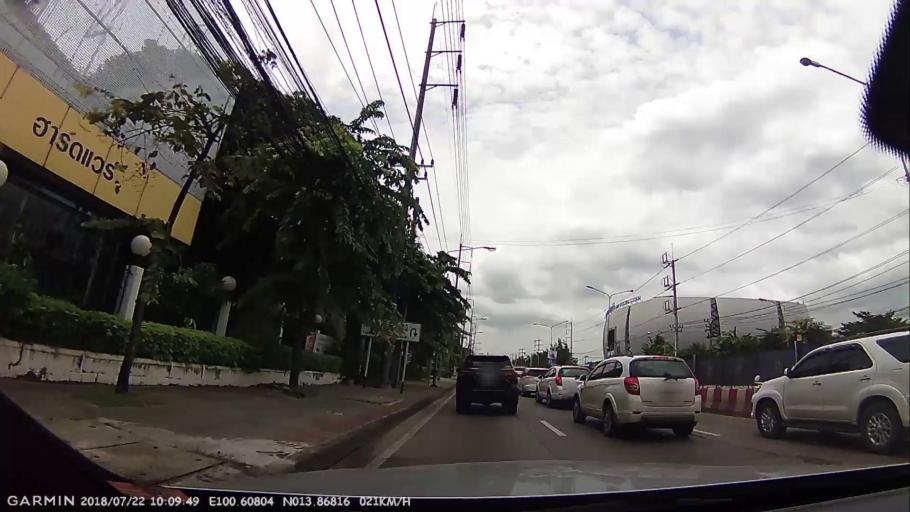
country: TH
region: Bangkok
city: Bang Khen
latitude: 13.8681
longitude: 100.6081
